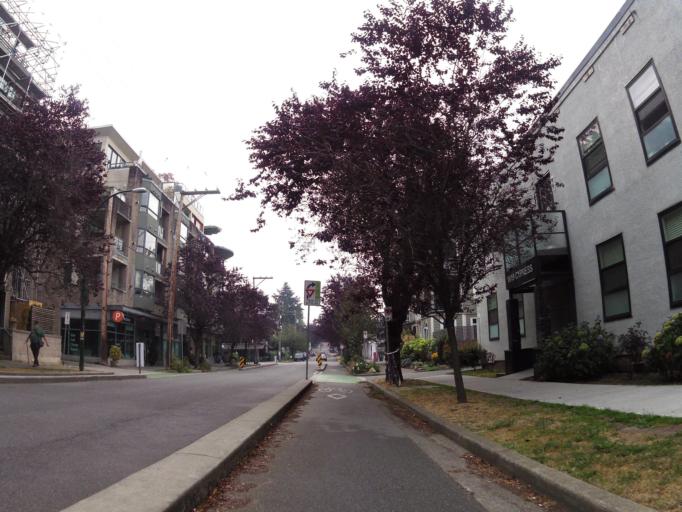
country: CA
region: British Columbia
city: West End
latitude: 49.2714
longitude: -123.1479
